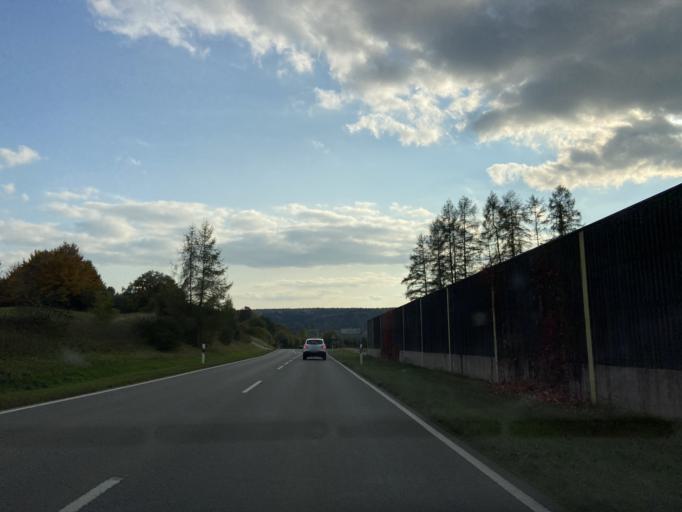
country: DE
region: Baden-Wuerttemberg
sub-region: Tuebingen Region
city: Sigmaringen
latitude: 48.0863
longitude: 9.2406
